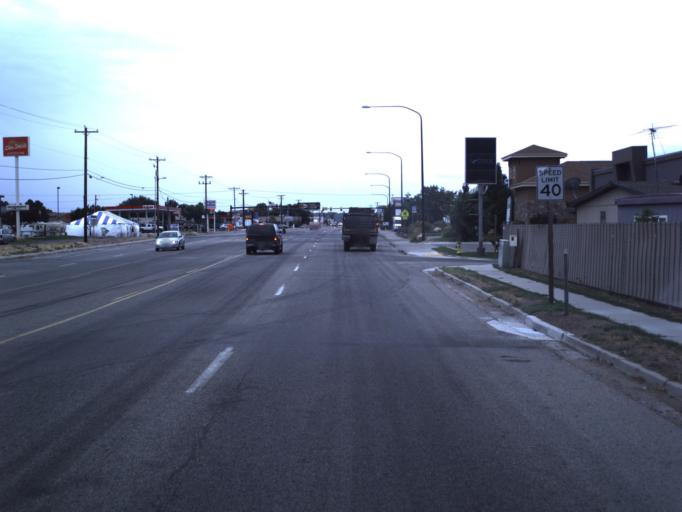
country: US
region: Utah
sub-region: Weber County
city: Ogden
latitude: 41.2468
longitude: -111.9783
